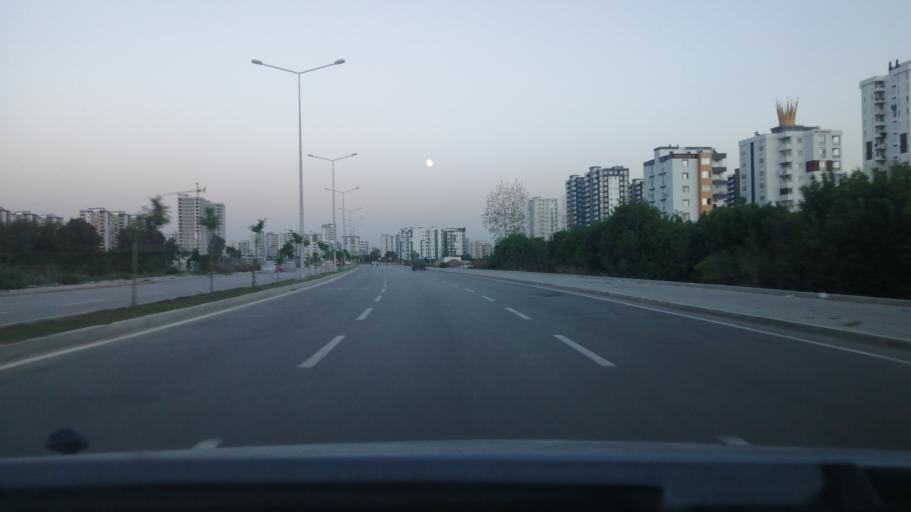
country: TR
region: Adana
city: Seyhan
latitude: 37.0152
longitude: 35.2534
